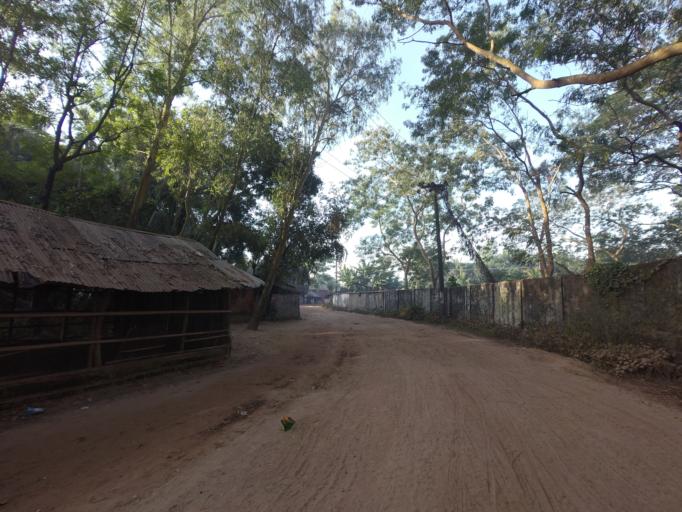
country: BD
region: Chittagong
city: Fatikchari
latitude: 22.5815
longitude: 91.6815
